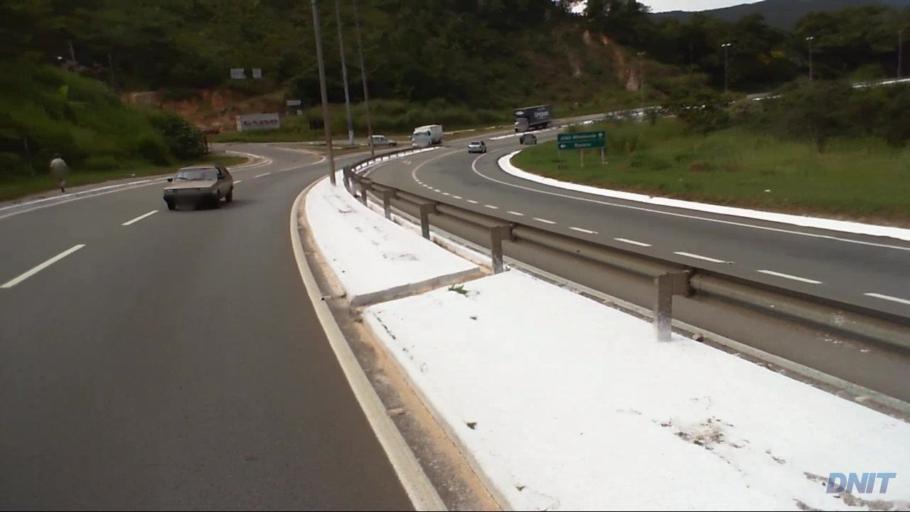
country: BR
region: Minas Gerais
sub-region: Santa Luzia
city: Santa Luzia
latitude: -19.7982
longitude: -43.7553
